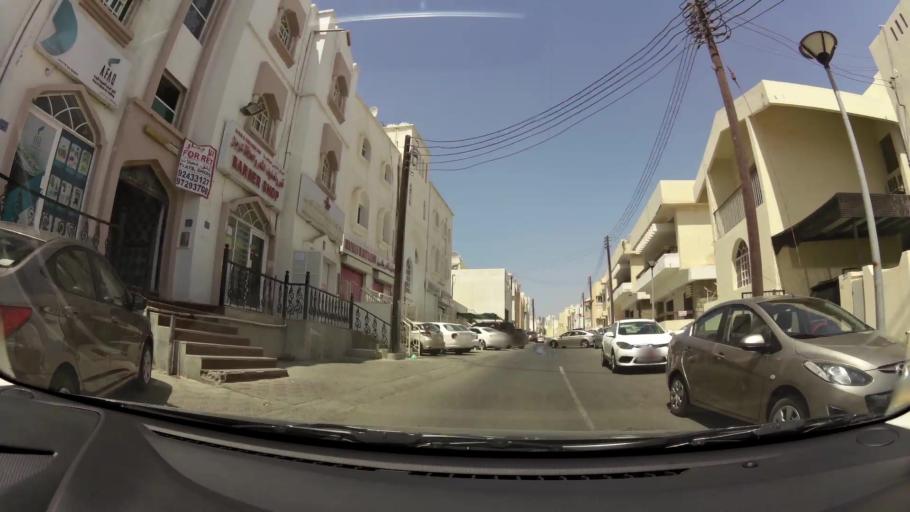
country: OM
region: Muhafazat Masqat
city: Muscat
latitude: 23.6192
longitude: 58.4965
